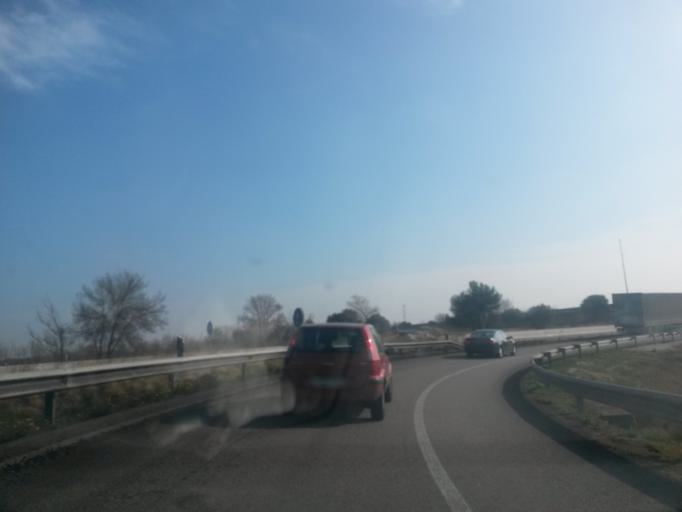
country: ES
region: Catalonia
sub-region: Provincia de Girona
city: Borrassa
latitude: 42.2271
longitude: 2.9375
